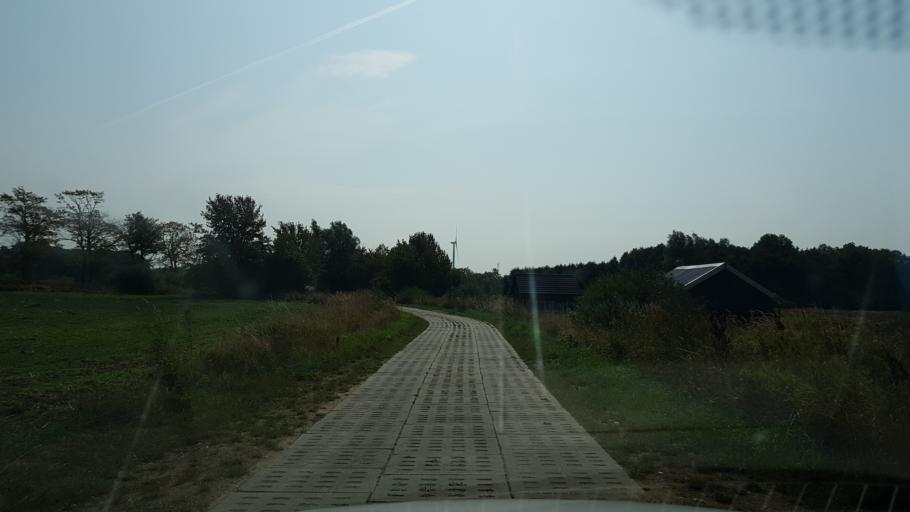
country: PL
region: West Pomeranian Voivodeship
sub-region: Powiat slawienski
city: Darlowo
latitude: 54.5030
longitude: 16.5044
